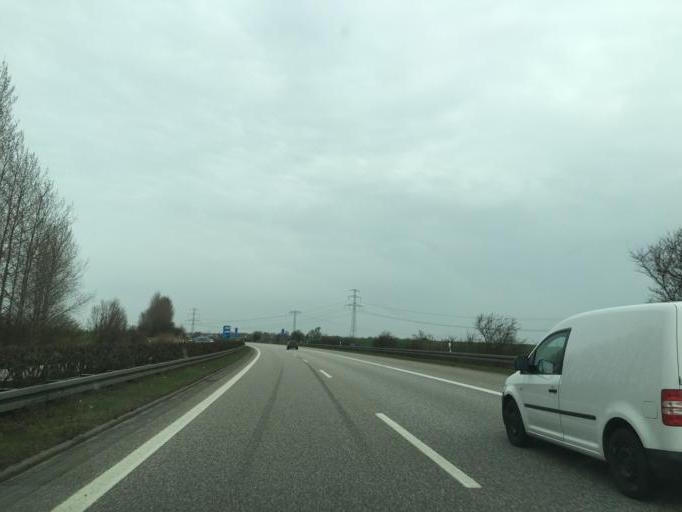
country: DE
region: Mecklenburg-Vorpommern
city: Bentwisch
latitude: 54.0956
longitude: 12.2011
